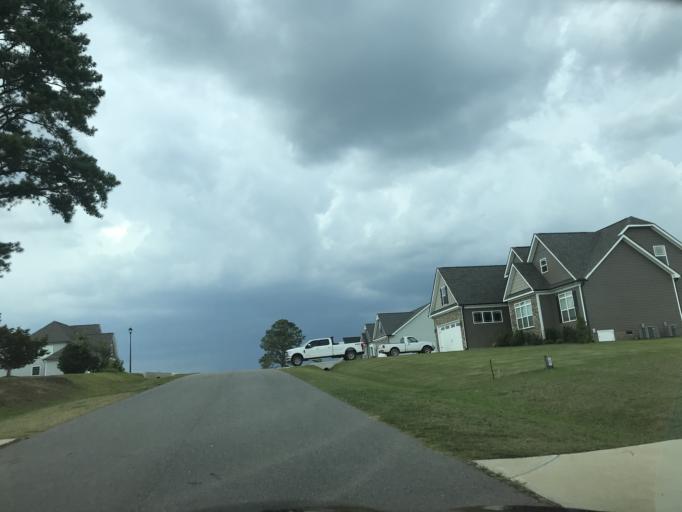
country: US
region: North Carolina
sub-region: Johnston County
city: Four Oaks
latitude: 35.5163
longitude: -78.5316
